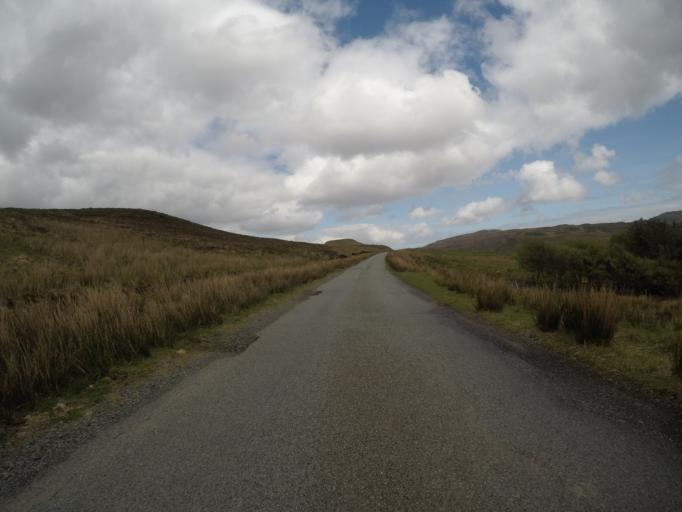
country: GB
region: Scotland
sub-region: Highland
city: Isle of Skye
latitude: 57.3706
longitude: -6.3813
